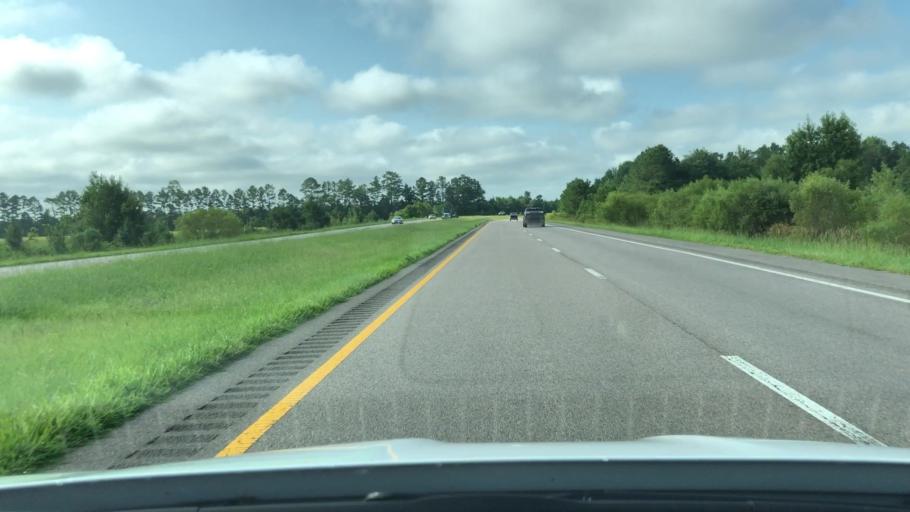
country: US
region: Virginia
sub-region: City of Portsmouth
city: Portsmouth Heights
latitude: 36.6816
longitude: -76.3473
